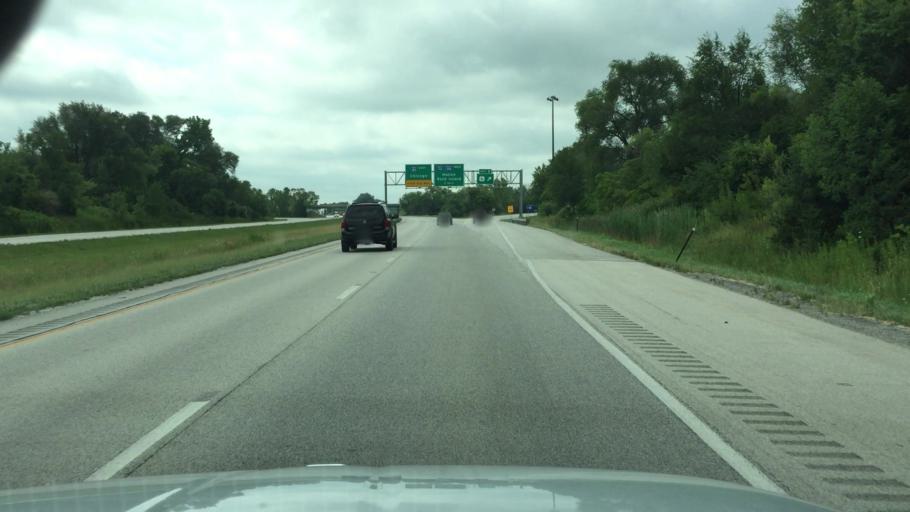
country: US
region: Illinois
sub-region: Henry County
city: Green Rock
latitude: 41.4594
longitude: -90.3383
